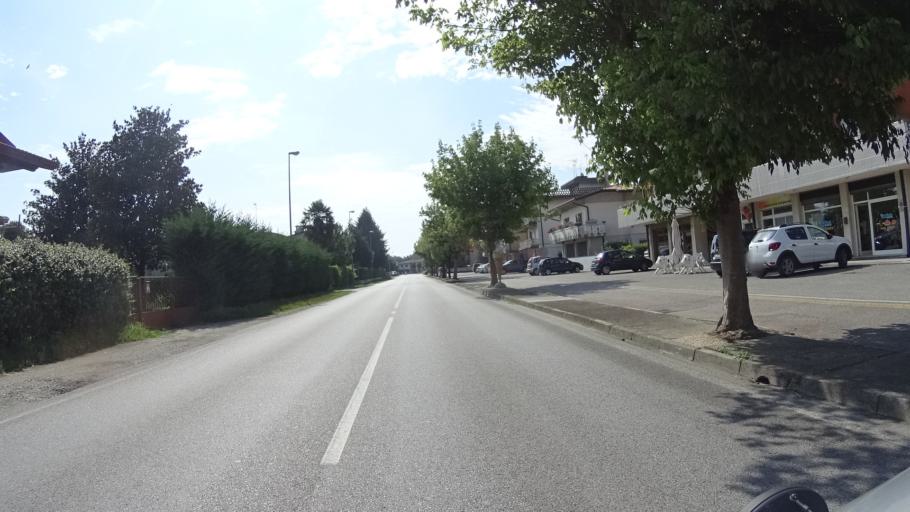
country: IT
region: Friuli Venezia Giulia
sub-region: Provincia di Udine
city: Latisana
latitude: 45.7732
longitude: 13.0160
